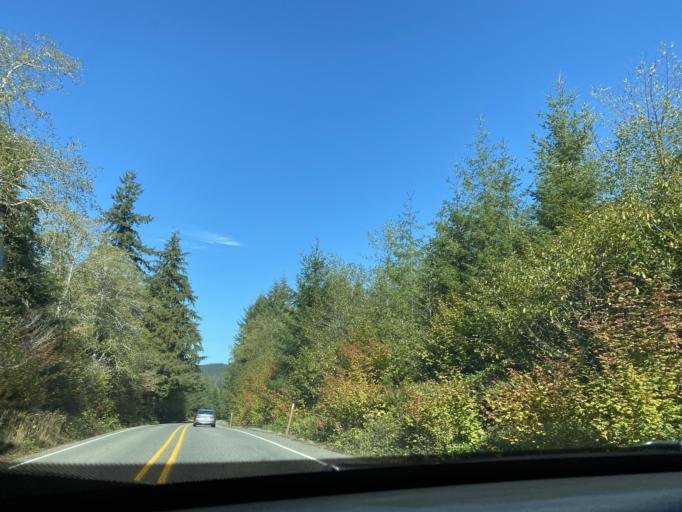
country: US
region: Washington
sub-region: Clallam County
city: Forks
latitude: 47.9462
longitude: -124.4624
